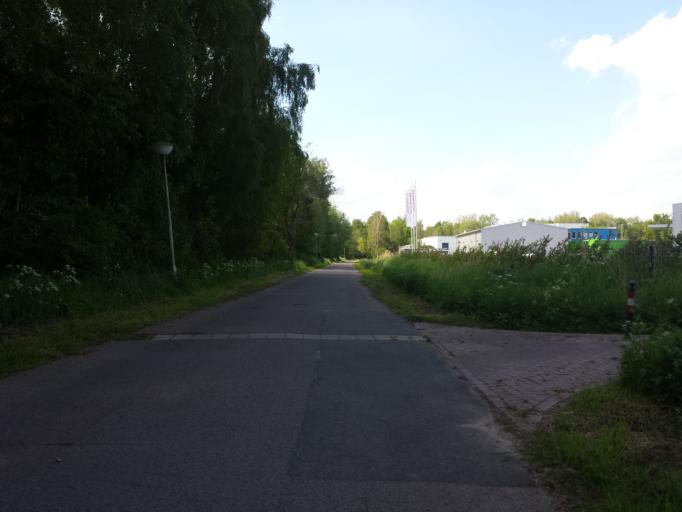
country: DE
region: Lower Saxony
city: Lilienthal
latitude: 53.1072
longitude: 8.8759
